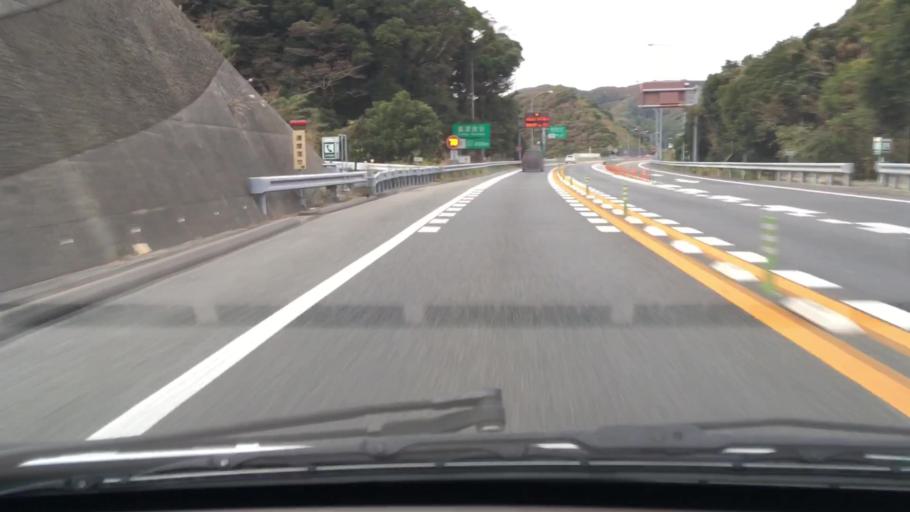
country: JP
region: Chiba
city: Futtsu
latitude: 35.1640
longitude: 139.8322
